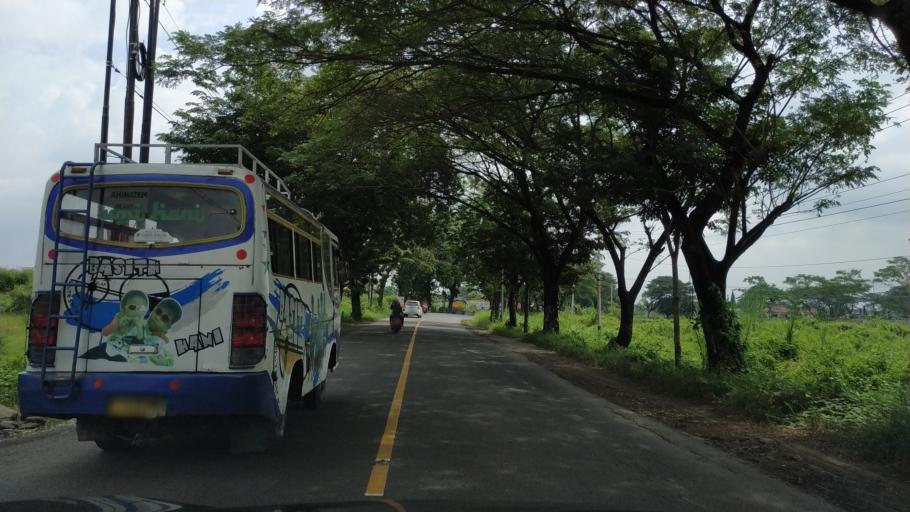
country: ID
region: Central Java
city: Lebaksiu
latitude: -7.0305
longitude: 109.1437
